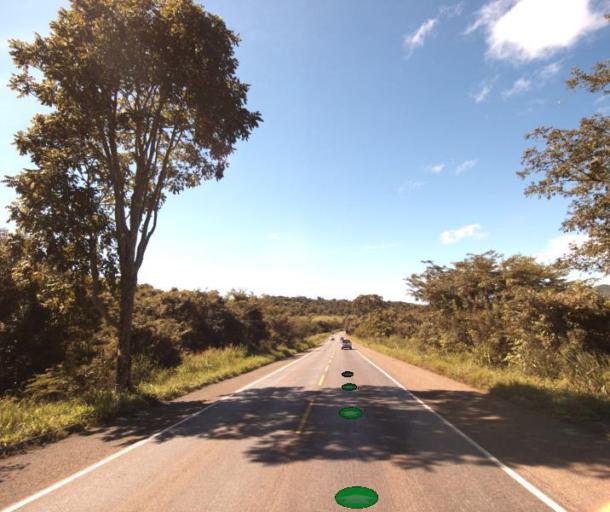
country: BR
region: Goias
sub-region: Rialma
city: Rialma
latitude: -15.2545
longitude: -49.5512
